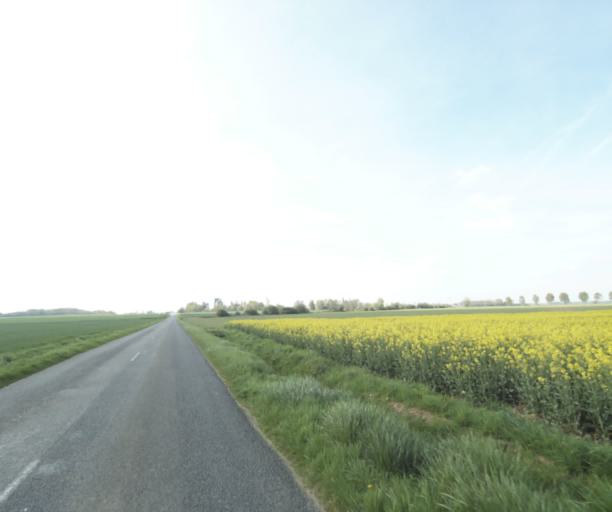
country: FR
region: Ile-de-France
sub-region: Departement de Seine-et-Marne
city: Nangis
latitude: 48.5729
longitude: 3.0122
